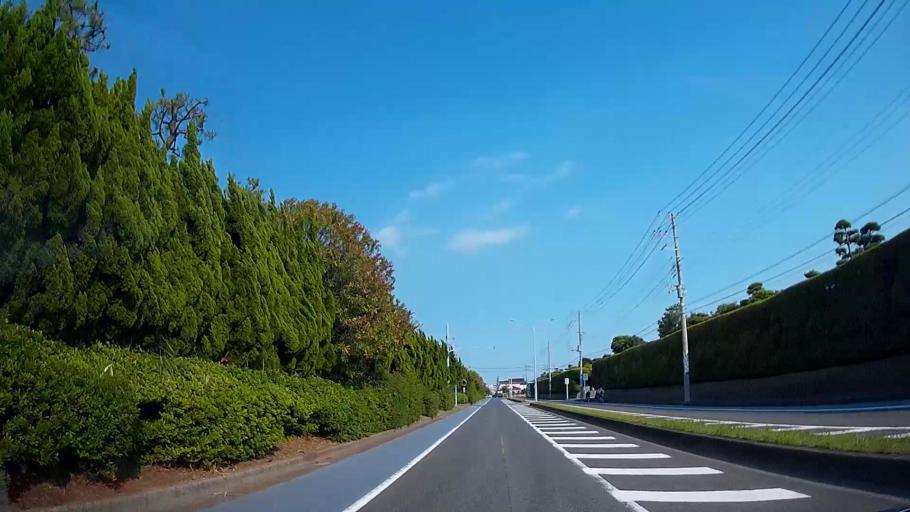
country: JP
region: Chiba
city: Chiba
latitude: 35.6318
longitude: 140.0514
